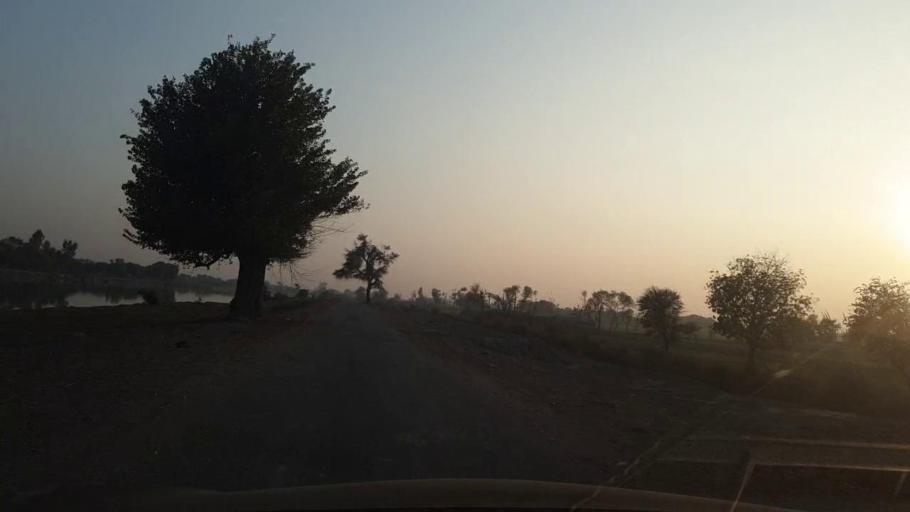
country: PK
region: Sindh
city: Ubauro
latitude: 28.2702
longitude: 69.7799
